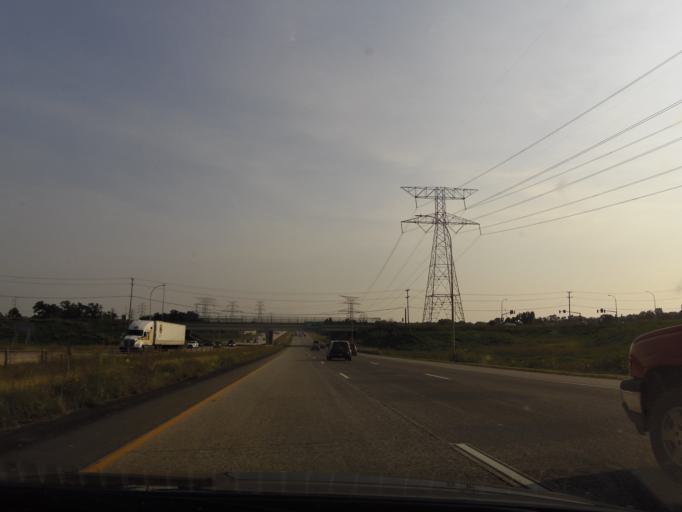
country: US
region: Minnesota
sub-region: Hennepin County
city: Plymouth
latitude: 44.9986
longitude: -93.4583
